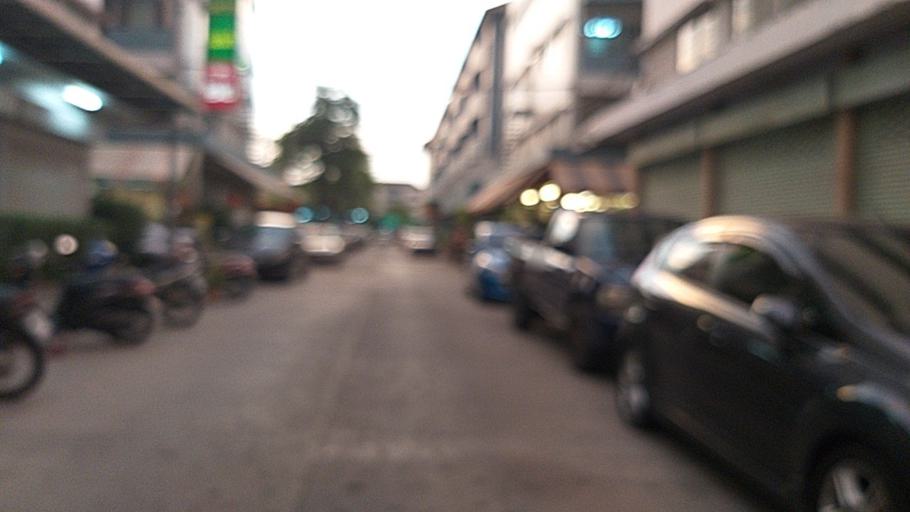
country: TH
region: Bangkok
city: Bang Na
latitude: 13.6674
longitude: 100.6830
